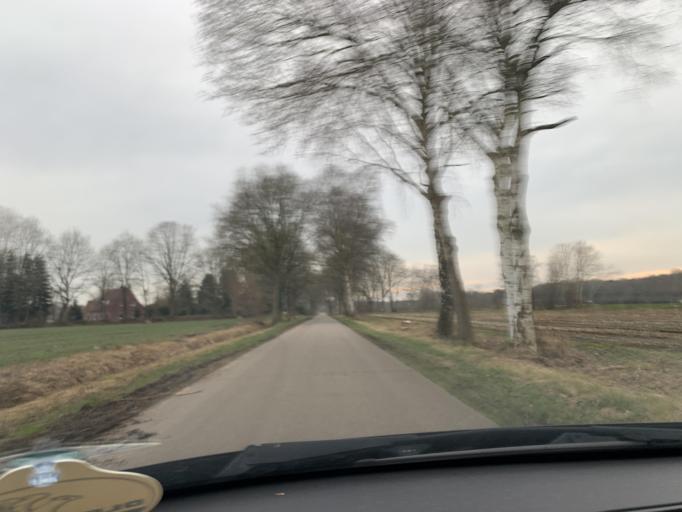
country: DE
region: Lower Saxony
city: Bad Zwischenahn
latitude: 53.2141
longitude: 8.0023
